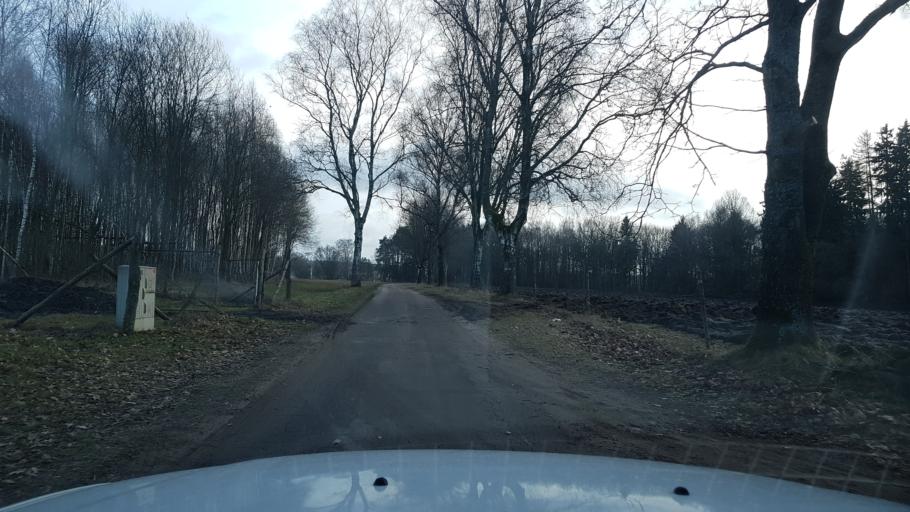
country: PL
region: West Pomeranian Voivodeship
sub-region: Powiat szczecinecki
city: Borne Sulinowo
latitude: 53.6269
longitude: 16.6128
